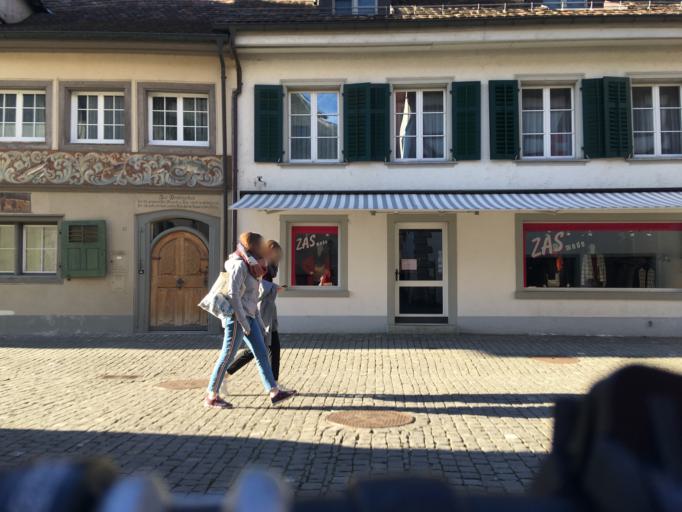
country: CH
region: Schaffhausen
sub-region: Bezirk Stein
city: Stein am Rhein
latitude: 47.6593
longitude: 8.8584
